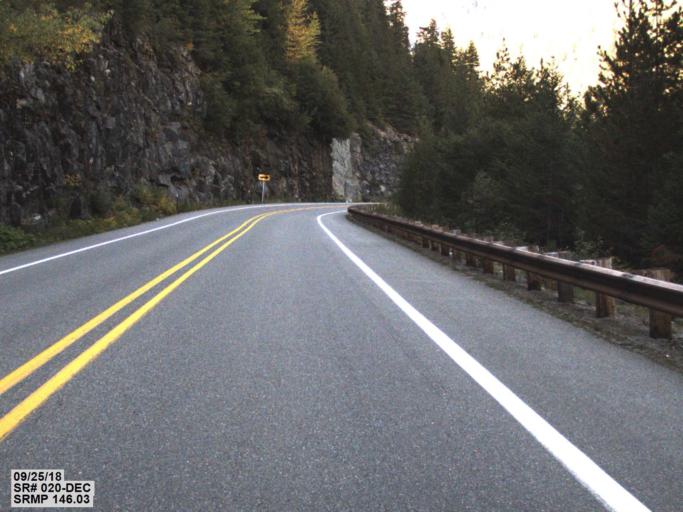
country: US
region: Washington
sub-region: Snohomish County
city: Darrington
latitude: 48.6531
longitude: -120.8586
